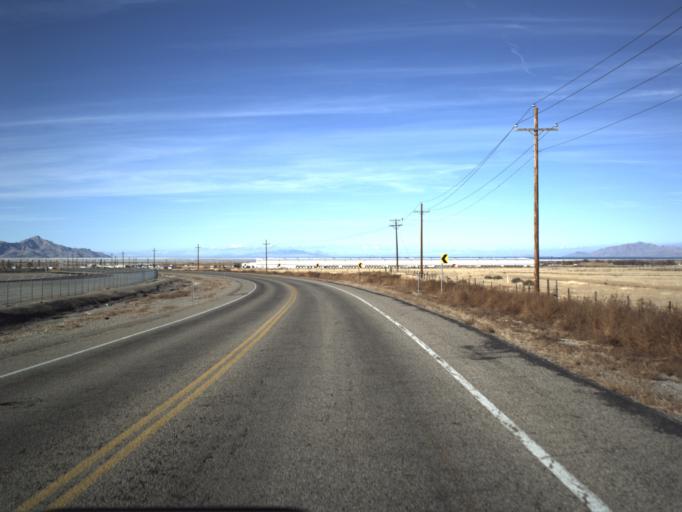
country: US
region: Utah
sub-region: Tooele County
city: Erda
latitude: 40.5764
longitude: -112.3674
